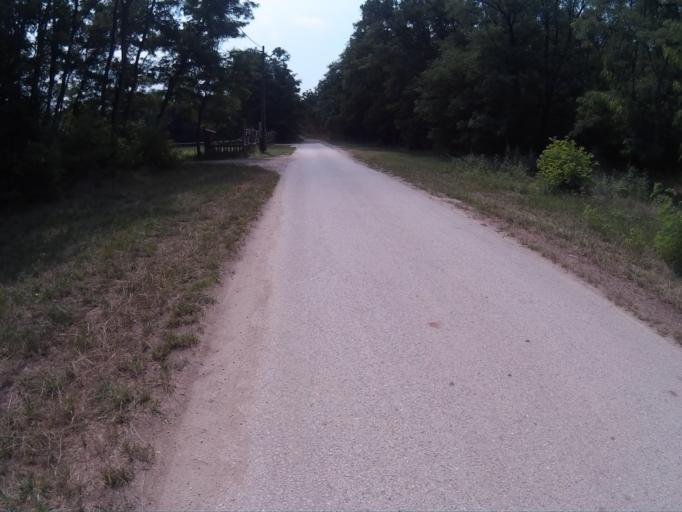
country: HU
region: Veszprem
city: Papa
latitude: 47.2926
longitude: 17.5997
